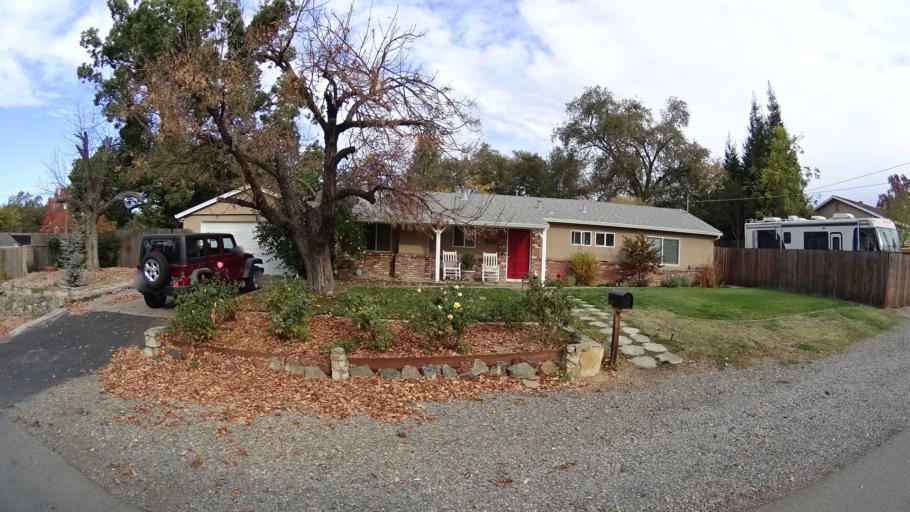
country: US
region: California
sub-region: Sacramento County
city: Citrus Heights
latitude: 38.7065
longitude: -121.2472
